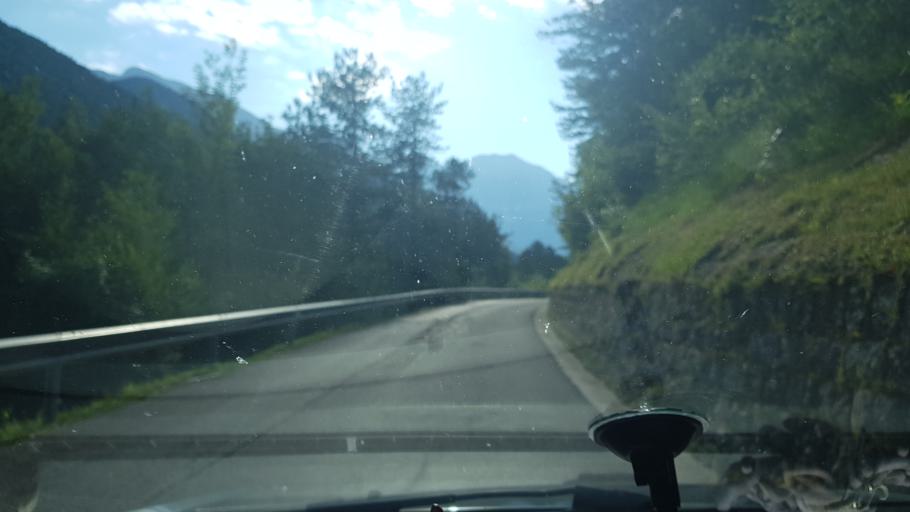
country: IT
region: Friuli Venezia Giulia
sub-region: Provincia di Udine
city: Prato
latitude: 46.3639
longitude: 13.3376
